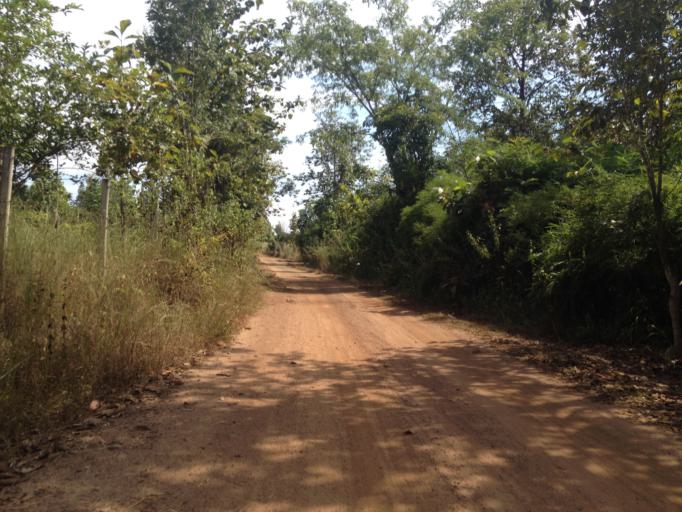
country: TH
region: Chiang Mai
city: Hang Dong
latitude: 18.7119
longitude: 98.8774
